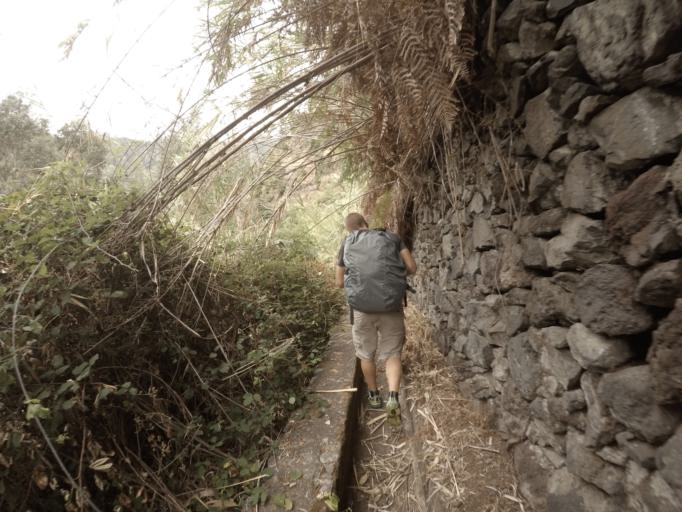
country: PT
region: Madeira
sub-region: Camara de Lobos
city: Curral das Freiras
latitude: 32.6826
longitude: -16.9597
